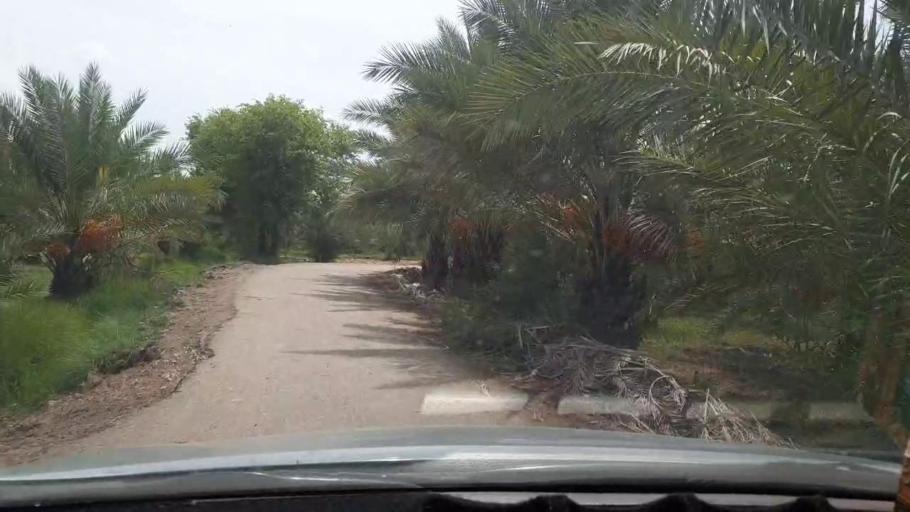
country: PK
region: Sindh
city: Khairpur
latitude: 27.4609
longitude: 68.8210
